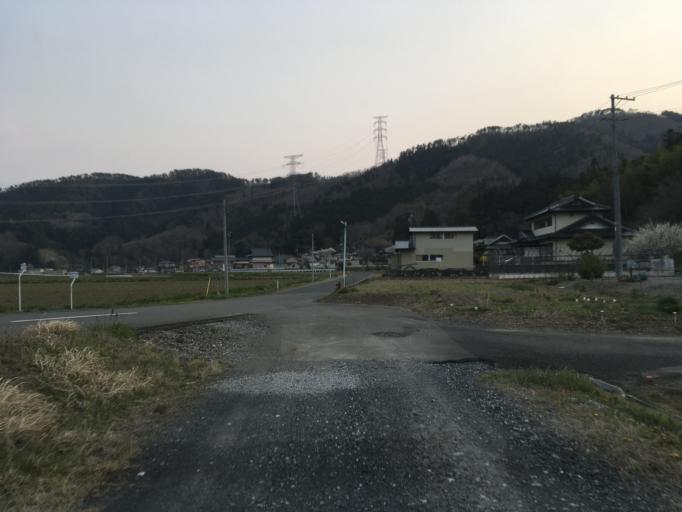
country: JP
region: Iwate
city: Ichinoseki
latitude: 38.9389
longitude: 141.2456
